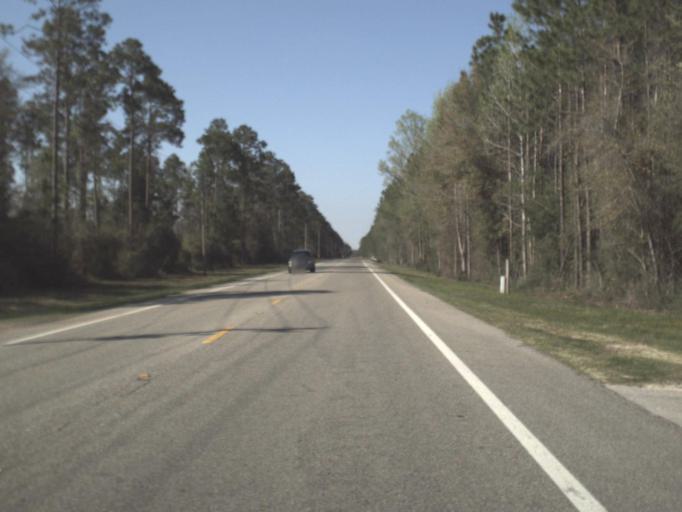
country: US
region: Florida
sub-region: Gulf County
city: Wewahitchka
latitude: 30.1859
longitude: -85.2059
